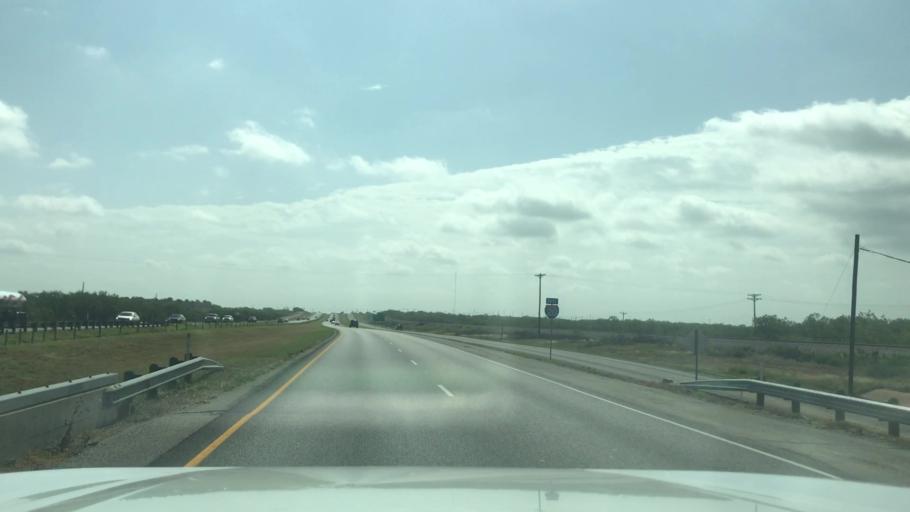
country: US
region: Texas
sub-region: Taylor County
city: Merkel
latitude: 32.4616
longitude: -99.9444
